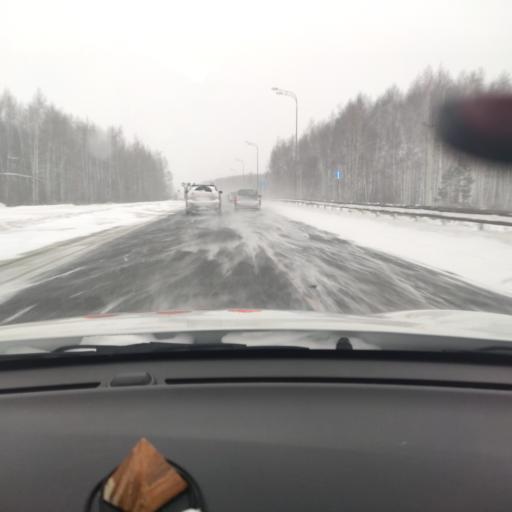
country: RU
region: Tatarstan
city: Verkhniy Uslon
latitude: 55.7097
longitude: 48.8892
